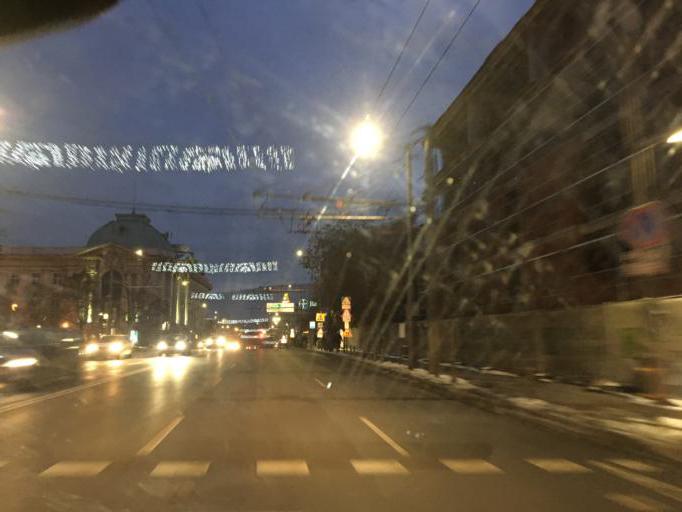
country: BG
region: Sofia-Capital
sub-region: Stolichna Obshtina
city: Sofia
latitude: 42.6956
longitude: 23.3350
